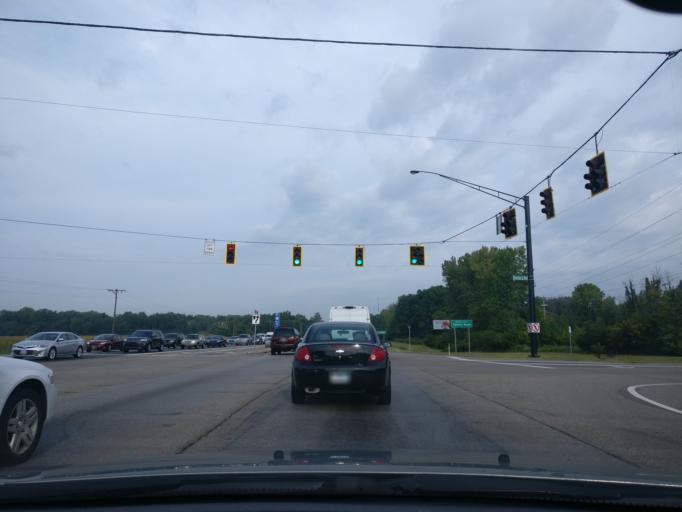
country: US
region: Ohio
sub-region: Greene County
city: Beavercreek
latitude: 39.7092
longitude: -84.0287
